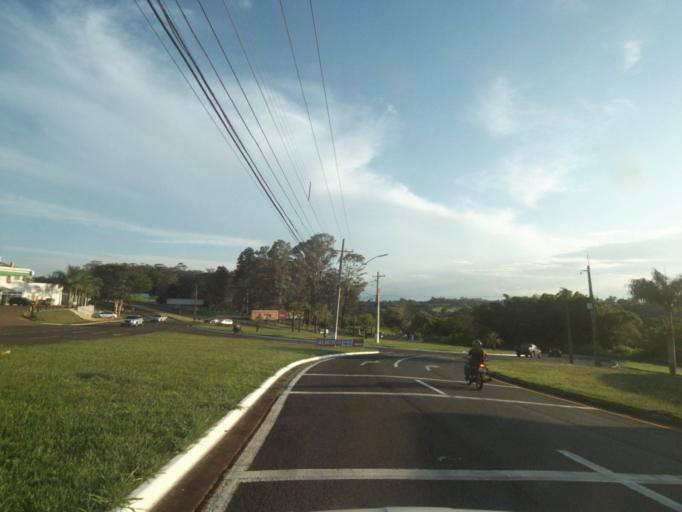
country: BR
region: Parana
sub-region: Londrina
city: Londrina
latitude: -23.3496
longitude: -51.1908
